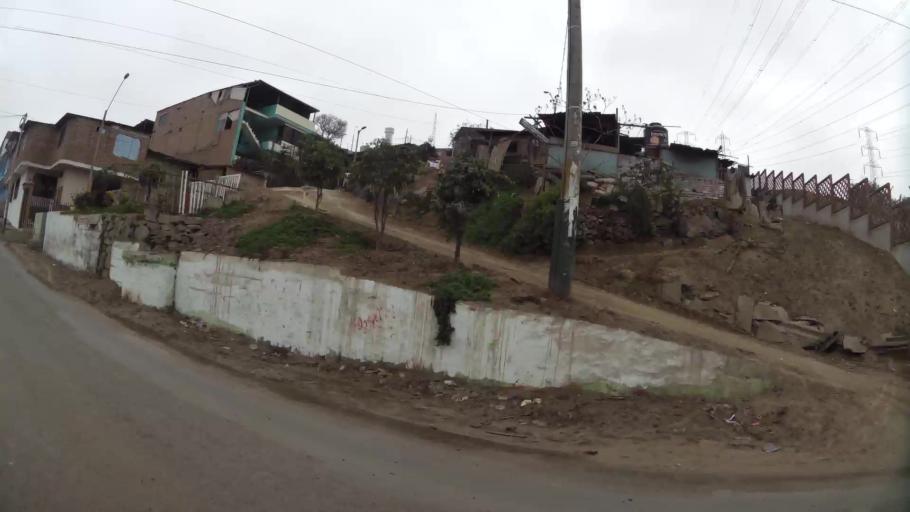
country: PE
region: Lima
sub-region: Lima
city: Surco
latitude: -12.1838
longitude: -76.9491
